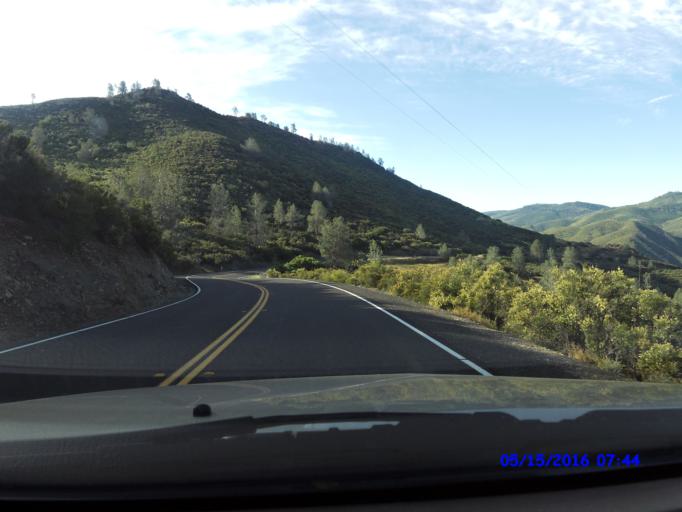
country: US
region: California
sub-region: Mariposa County
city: Mariposa
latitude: 37.6387
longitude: -120.1523
